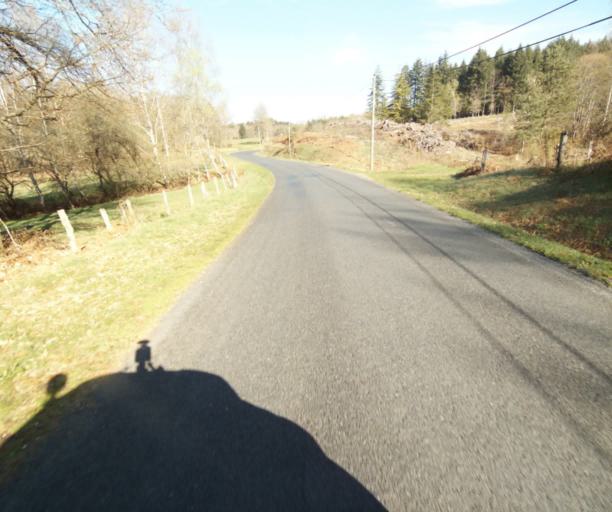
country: FR
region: Limousin
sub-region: Departement de la Correze
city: Correze
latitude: 45.2861
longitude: 1.8737
